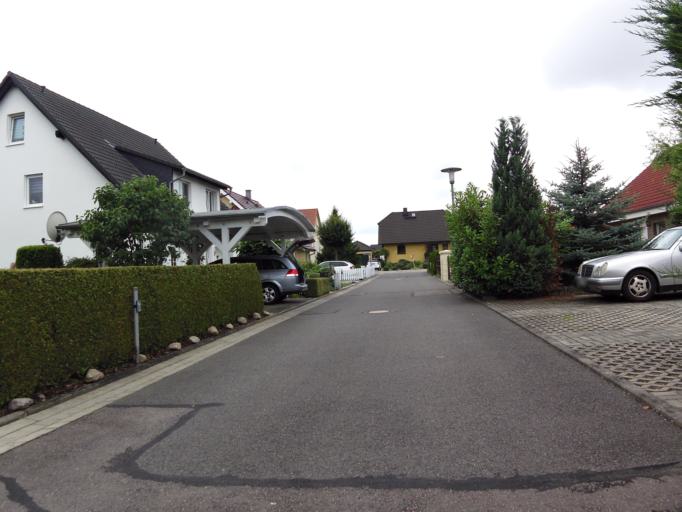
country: DE
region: Saxony
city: Taucha
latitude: 51.3517
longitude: 12.4863
